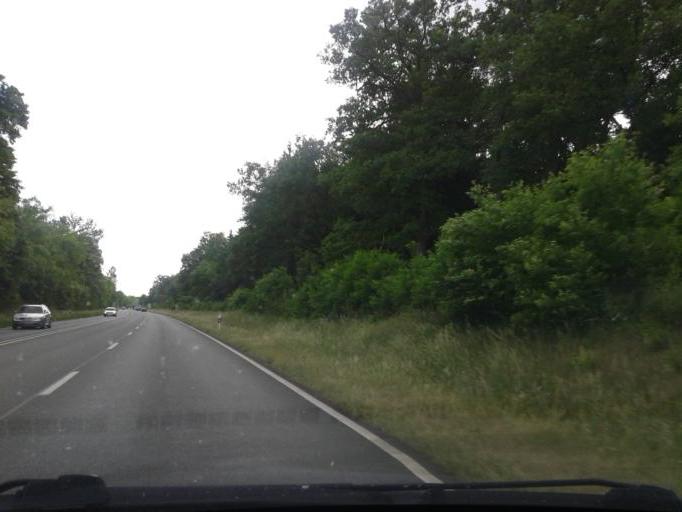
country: DE
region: North Rhine-Westphalia
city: Bad Lippspringe
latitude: 51.7751
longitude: 8.7765
